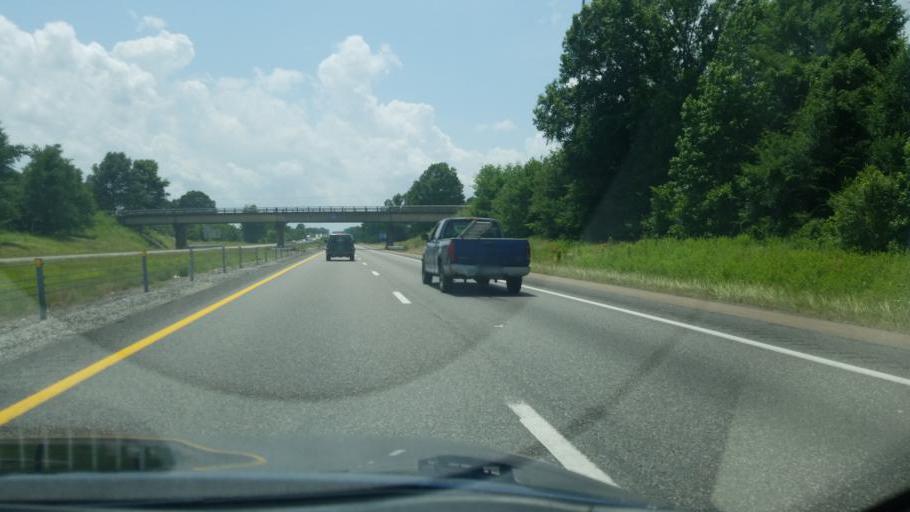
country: US
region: Tennessee
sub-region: Madison County
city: Jackson
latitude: 35.6393
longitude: -88.9283
